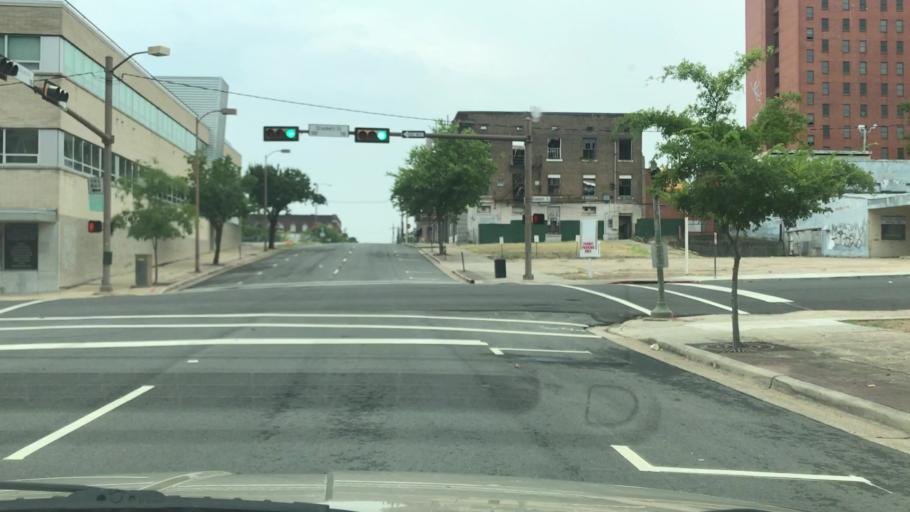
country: US
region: Louisiana
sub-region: Caddo Parish
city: Shreveport
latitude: 32.5100
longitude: -93.7502
